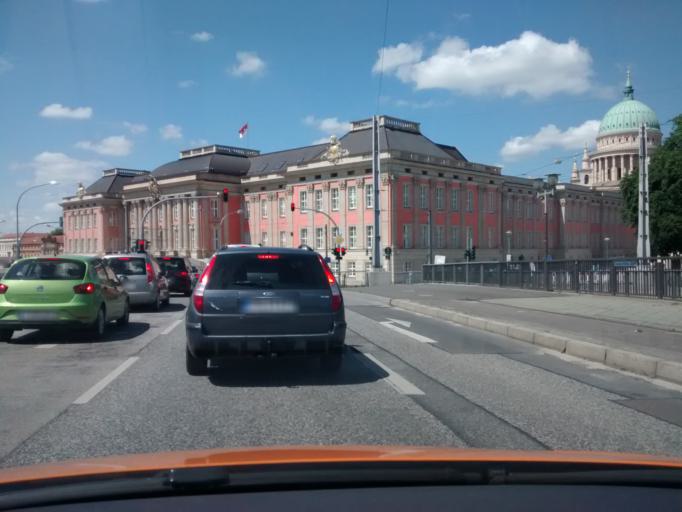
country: DE
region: Brandenburg
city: Potsdam
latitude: 52.3937
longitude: 13.0616
